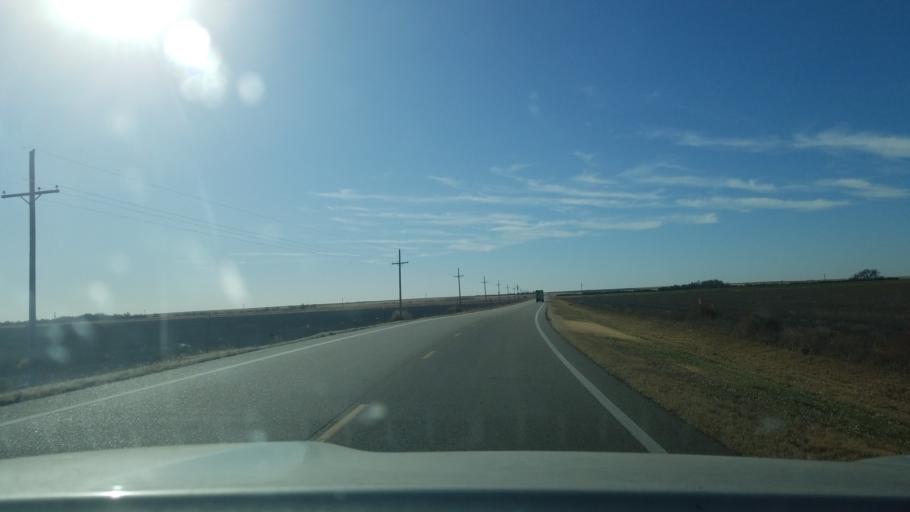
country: US
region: Kansas
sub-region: Ness County
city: Ness City
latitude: 38.4260
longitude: -99.8988
